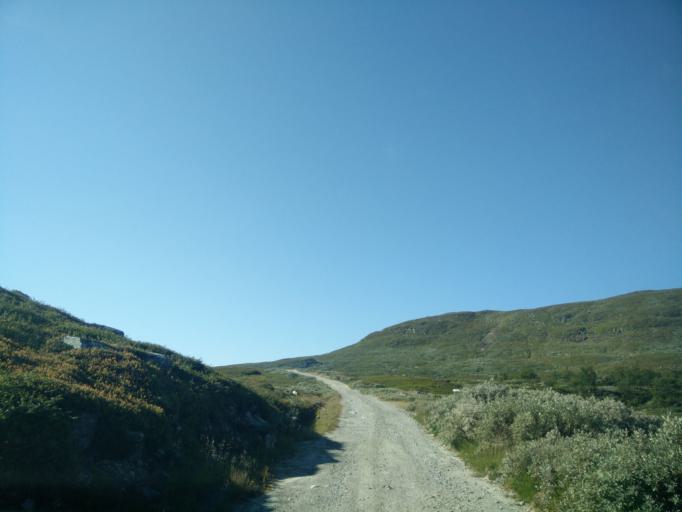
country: NO
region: Sor-Trondelag
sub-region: Tydal
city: Aas
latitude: 62.5714
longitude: 12.1980
